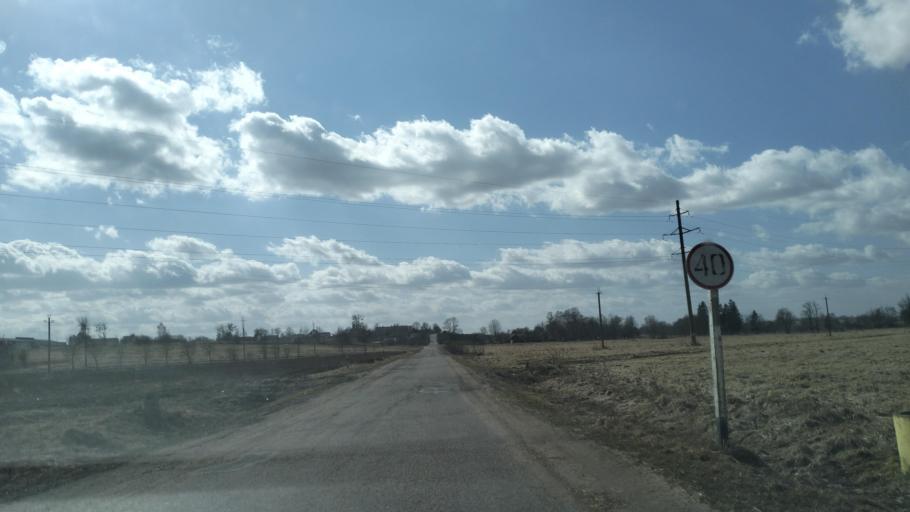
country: BY
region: Grodnenskaya
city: Karelichy
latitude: 53.6608
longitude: 26.1132
